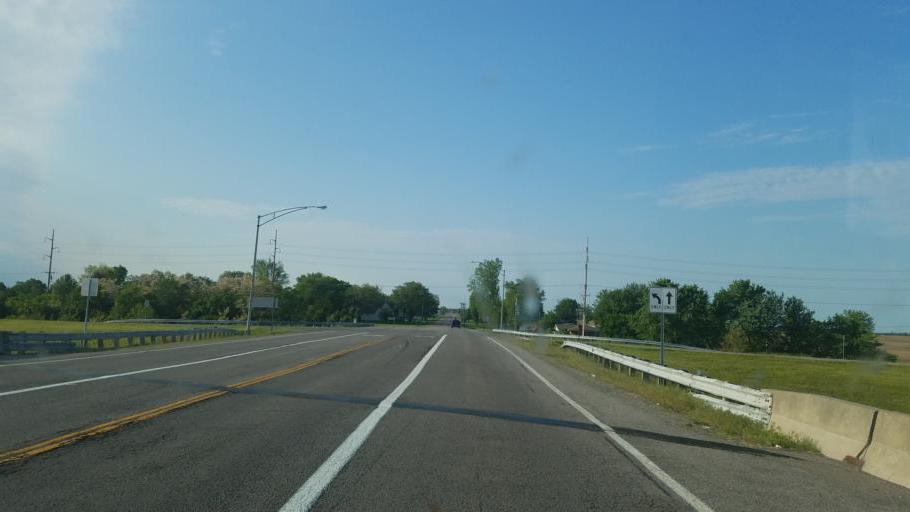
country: US
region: Ohio
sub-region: Fayette County
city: Washington Court House
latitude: 39.5145
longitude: -83.4427
